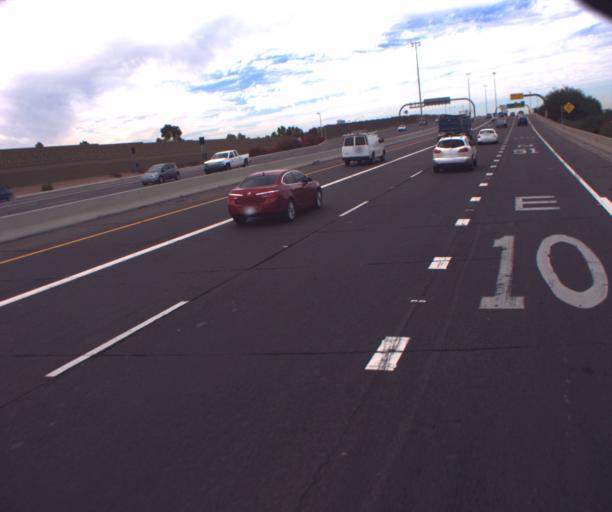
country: US
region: Arizona
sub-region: Maricopa County
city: Phoenix
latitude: 33.4622
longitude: -112.0260
